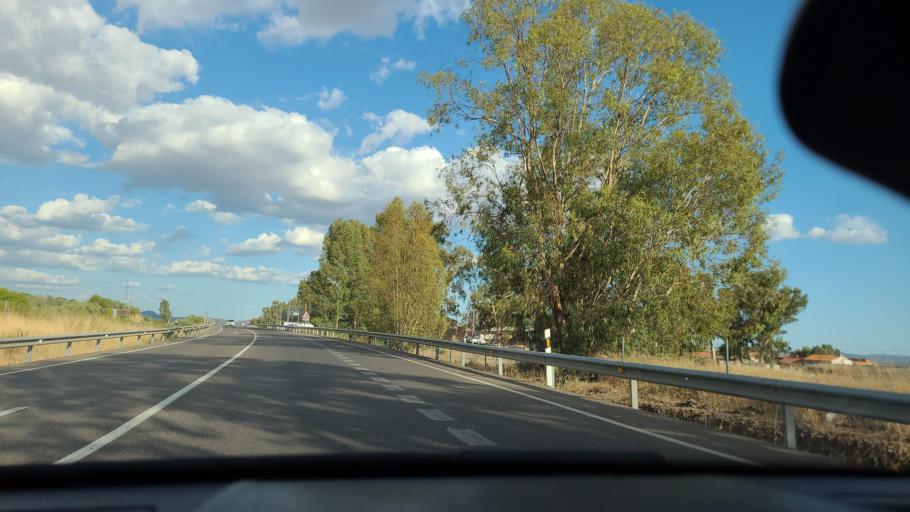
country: ES
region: Andalusia
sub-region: Province of Cordoba
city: Penarroya-Pueblonuevo
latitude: 38.2981
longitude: -5.2495
